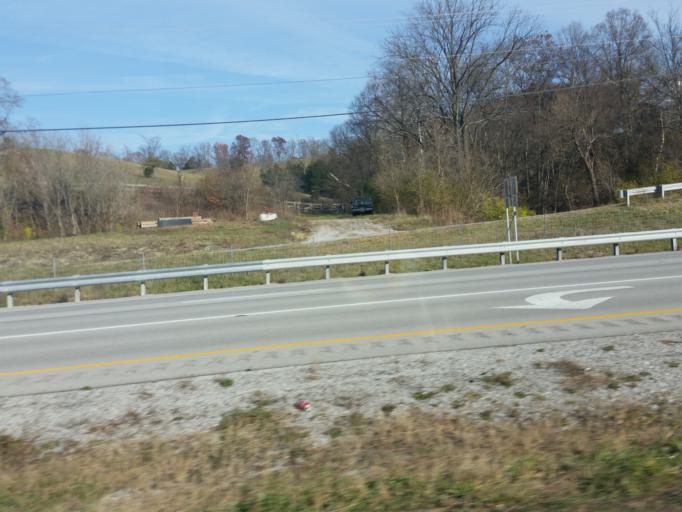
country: US
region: Kentucky
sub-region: Campbell County
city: Claryville
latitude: 38.8637
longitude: -84.3921
